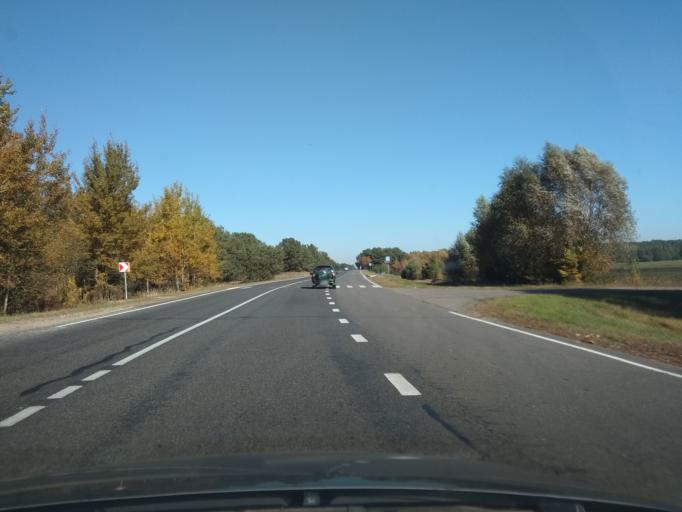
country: BY
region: Brest
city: Kobryn
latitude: 52.1301
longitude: 24.3052
